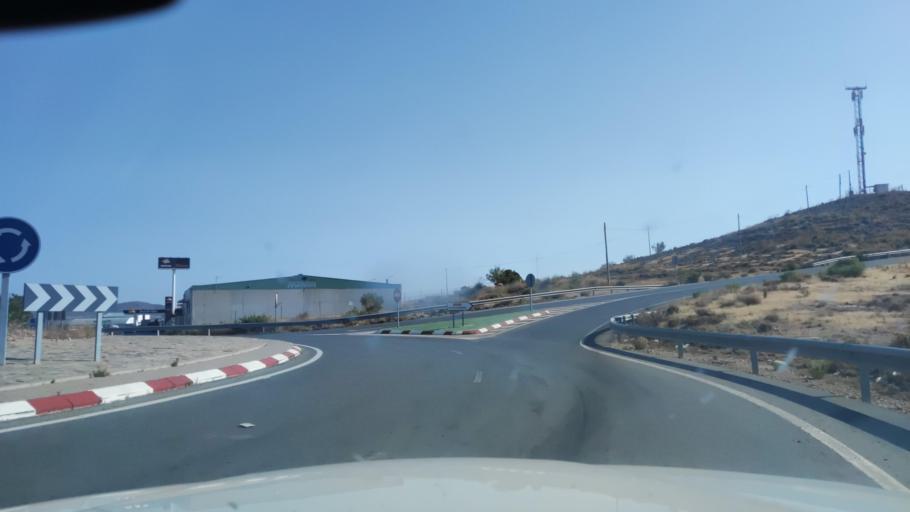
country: ES
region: Castille-La Mancha
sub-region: Provincia de Albacete
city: Tobarra
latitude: 38.6045
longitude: -1.6815
